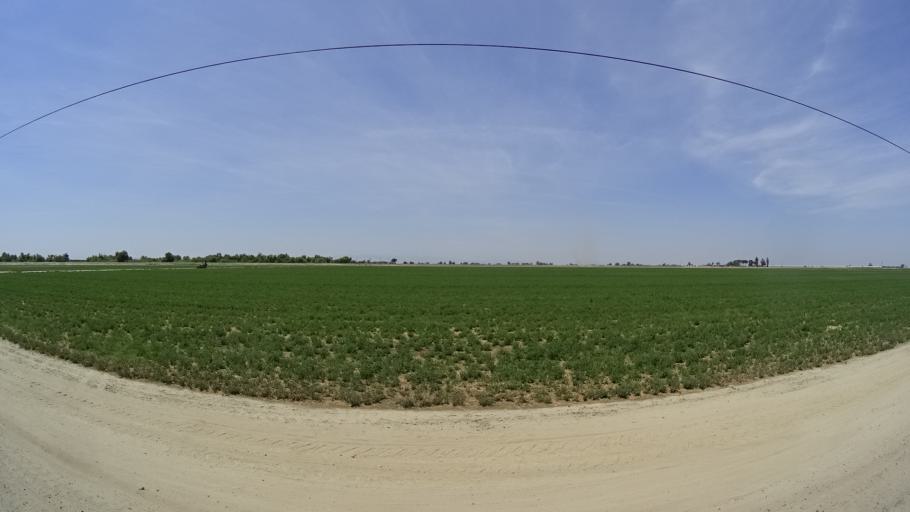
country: US
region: California
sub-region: Fresno County
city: Riverdale
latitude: 36.3955
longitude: -119.9052
